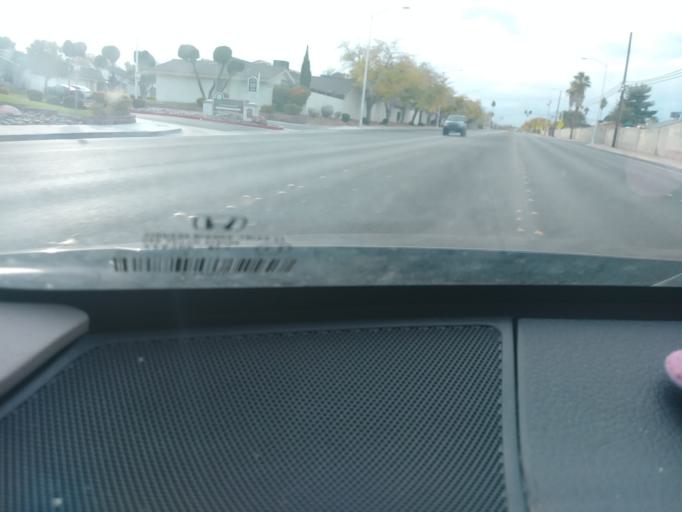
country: US
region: Nevada
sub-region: Clark County
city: Spring Valley
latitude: 36.1809
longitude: -115.2184
